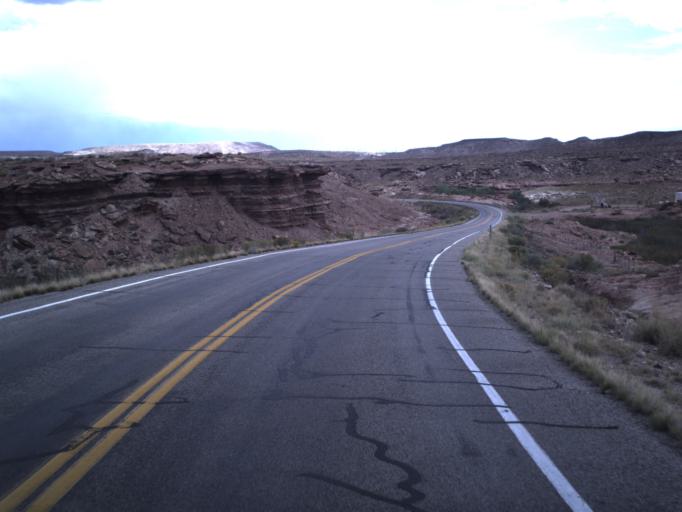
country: US
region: Utah
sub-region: San Juan County
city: Blanding
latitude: 37.2914
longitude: -109.4098
